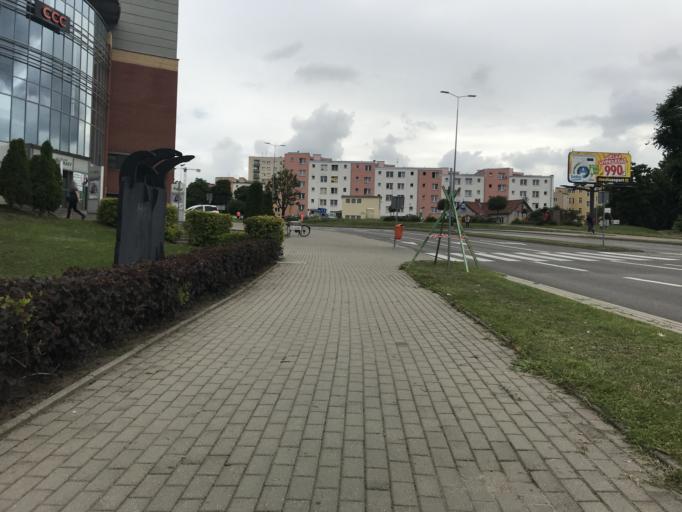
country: PL
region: Warmian-Masurian Voivodeship
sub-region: Powiat elblaski
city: Elblag
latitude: 54.1655
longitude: 19.4008
